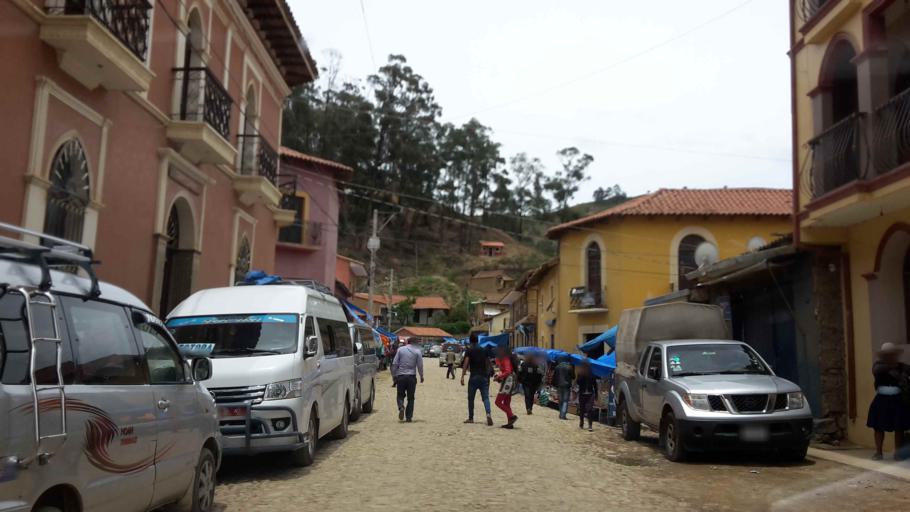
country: BO
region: Cochabamba
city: Totora
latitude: -17.7354
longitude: -65.1919
